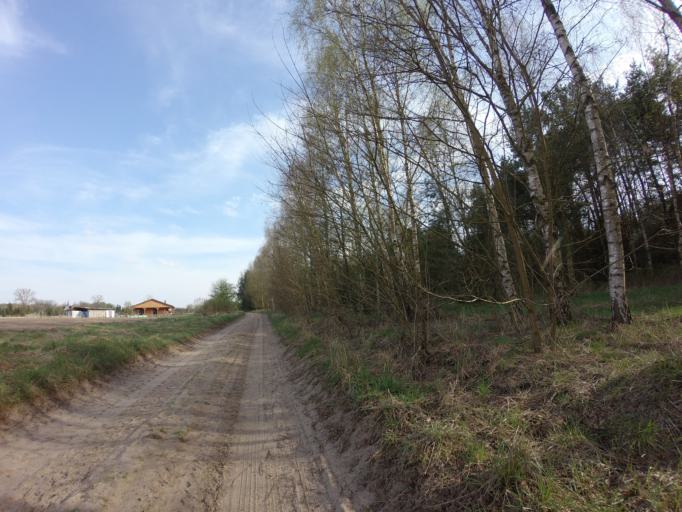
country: PL
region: West Pomeranian Voivodeship
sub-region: Powiat choszczenski
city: Recz
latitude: 53.1938
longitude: 15.4989
